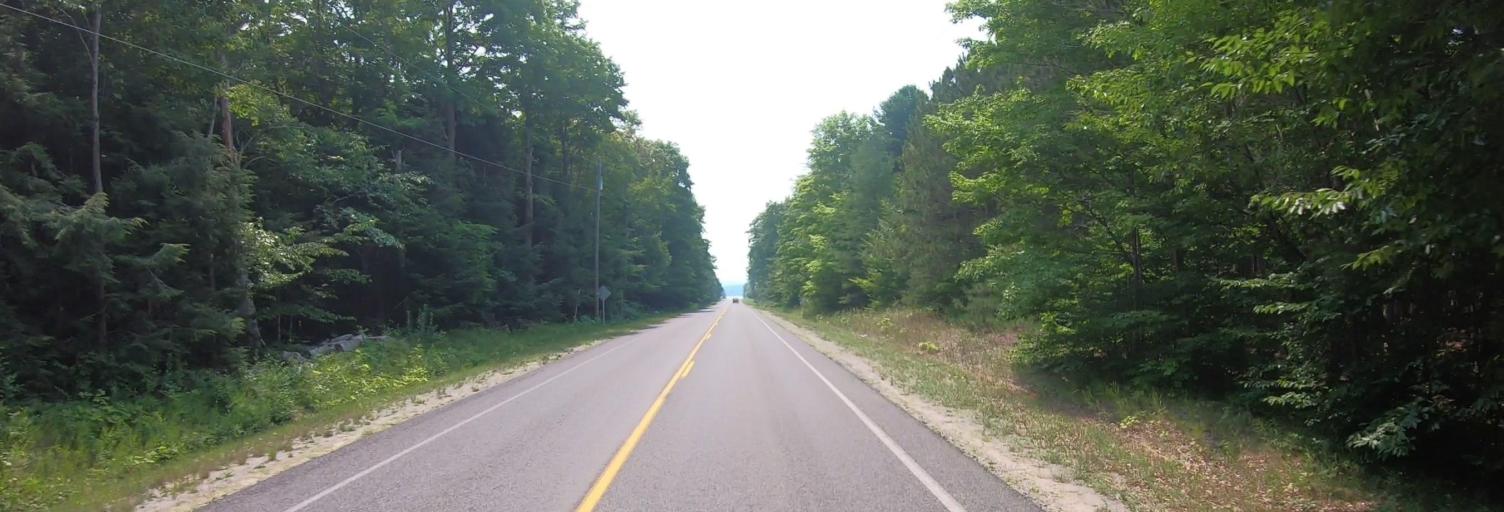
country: US
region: Michigan
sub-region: Leelanau County
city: Leland
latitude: 45.1580
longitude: -85.5885
